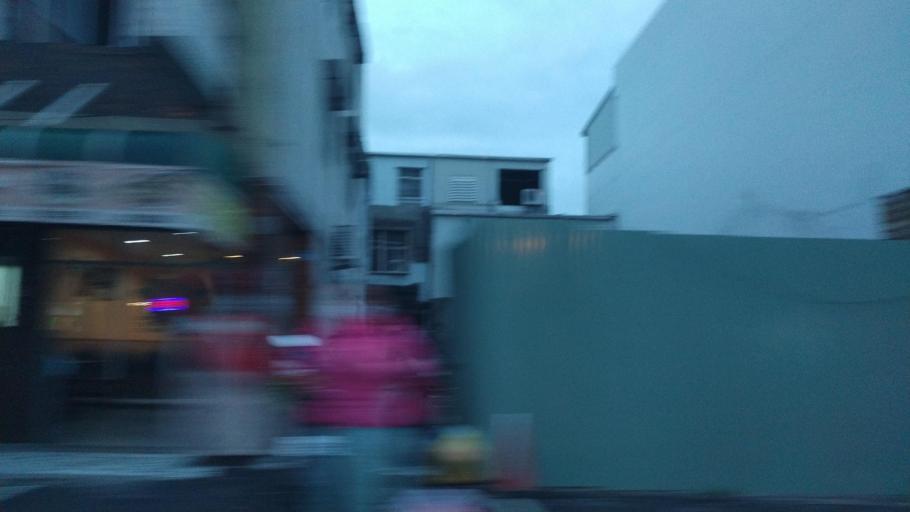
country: TW
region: Taiwan
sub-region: Hualien
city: Hualian
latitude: 23.9767
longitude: 121.6014
